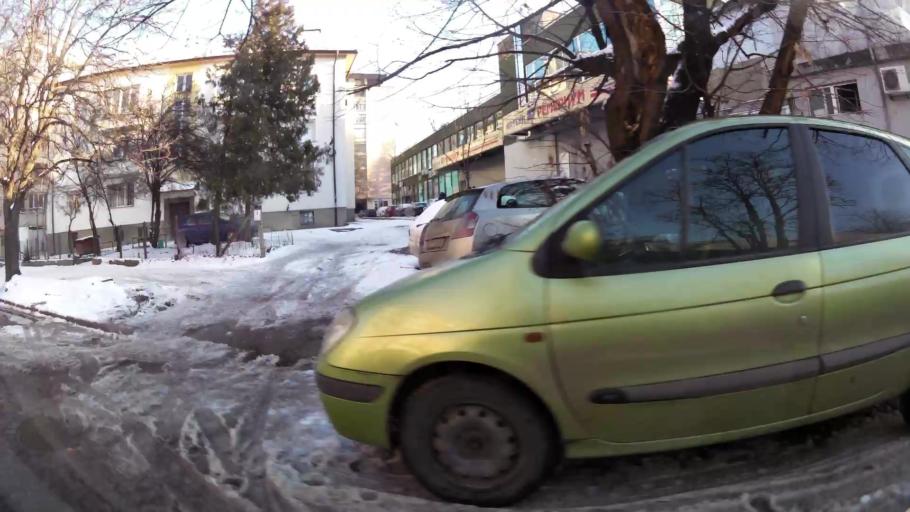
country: BG
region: Sofia-Capital
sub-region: Stolichna Obshtina
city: Sofia
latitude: 42.6843
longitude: 23.3537
